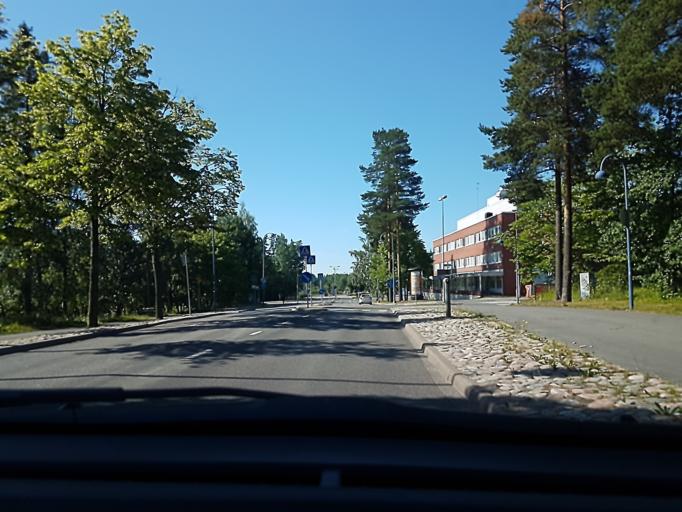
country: FI
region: Uusimaa
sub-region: Helsinki
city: Vantaa
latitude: 60.3200
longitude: 25.0618
